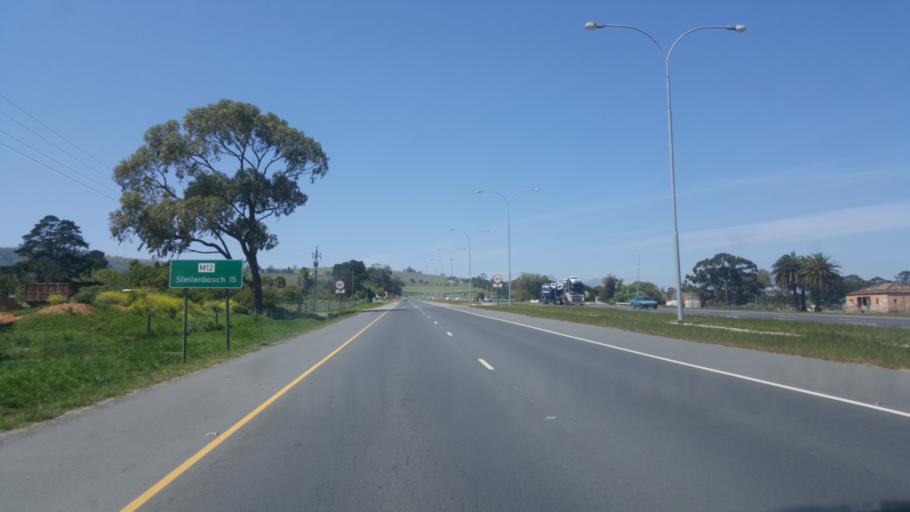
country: ZA
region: Western Cape
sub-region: City of Cape Town
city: Kraaifontein
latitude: -33.9505
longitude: 18.7086
